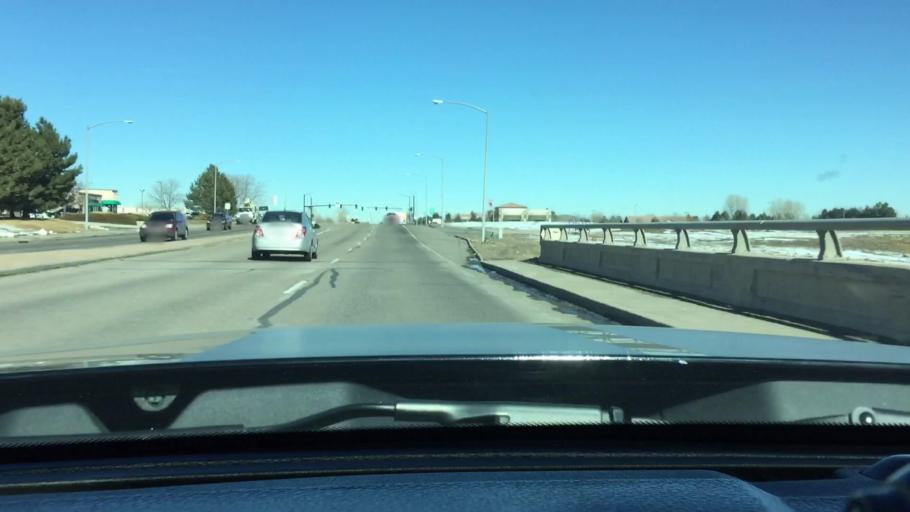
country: US
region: Colorado
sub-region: Broomfield County
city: Broomfield
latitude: 39.8970
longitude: -105.0529
